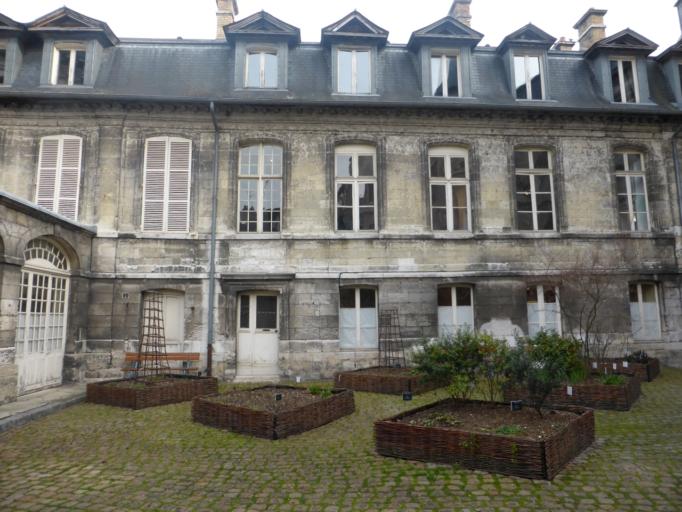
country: FR
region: Champagne-Ardenne
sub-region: Departement de l'Aube
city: Troyes
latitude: 48.2946
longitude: 4.0717
